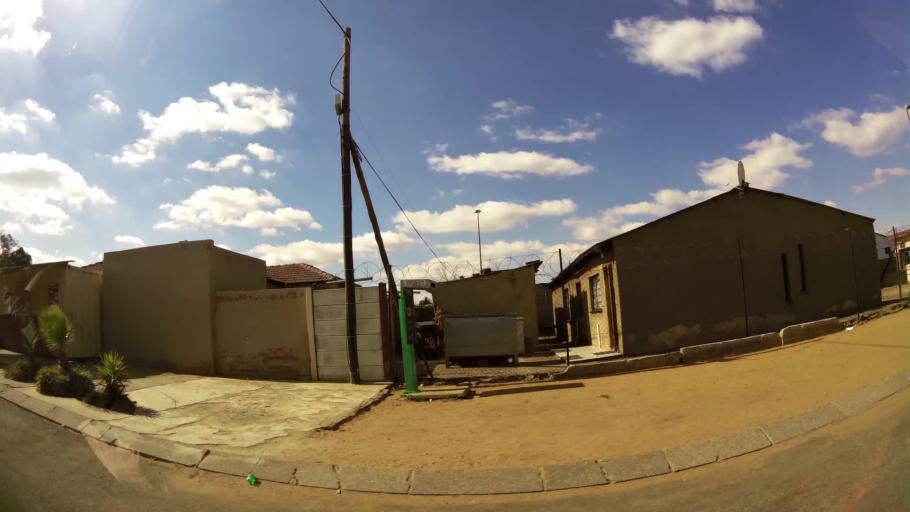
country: ZA
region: Gauteng
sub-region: West Rand District Municipality
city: Krugersdorp
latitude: -26.1407
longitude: 27.7969
